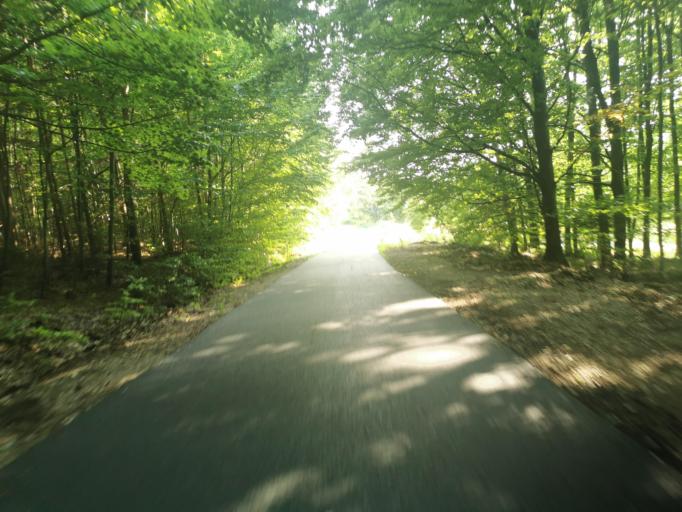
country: SK
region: Trenciansky
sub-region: Okres Myjava
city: Myjava
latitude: 48.8245
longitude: 17.6091
